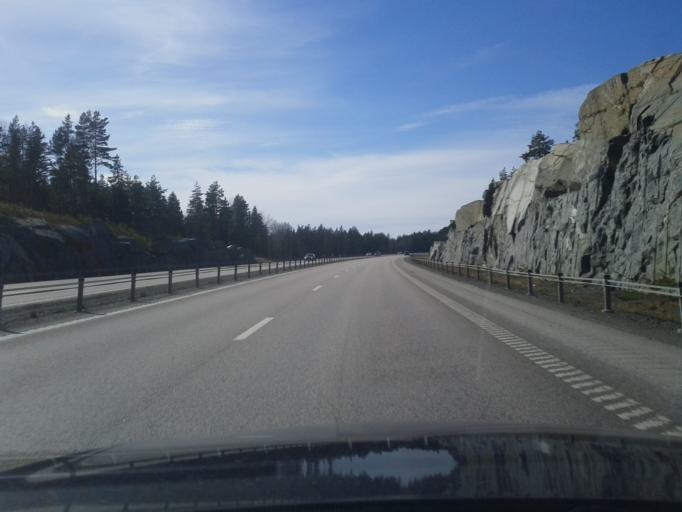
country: SE
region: Uppsala
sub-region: Enkopings Kommun
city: Hummelsta
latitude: 59.6409
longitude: 16.9548
